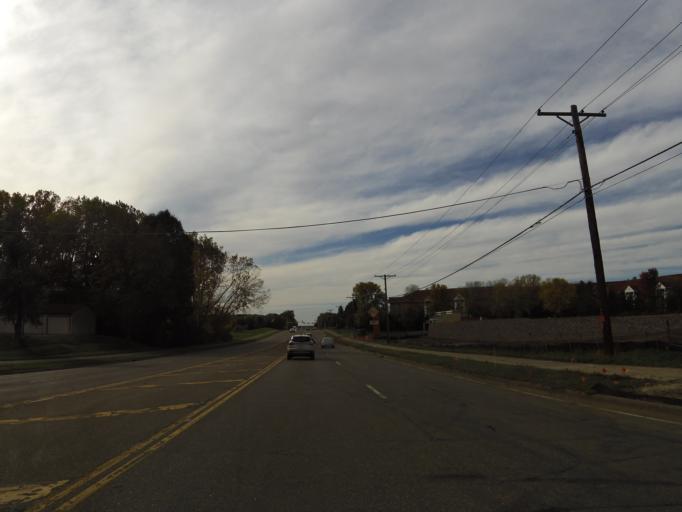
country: US
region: Minnesota
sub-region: Dakota County
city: Eagan
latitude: 44.8336
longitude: -93.1757
